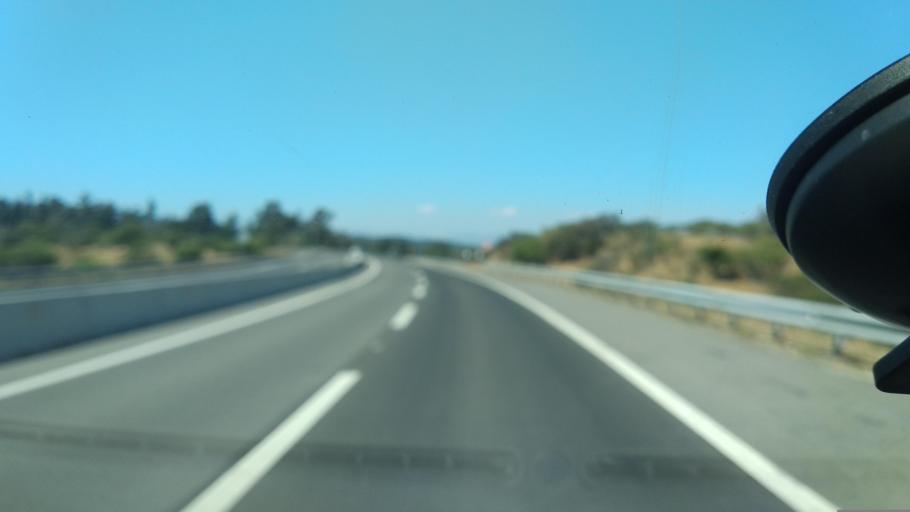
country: CL
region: Valparaiso
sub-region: Provincia de Marga Marga
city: Limache
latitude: -32.9854
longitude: -71.3187
